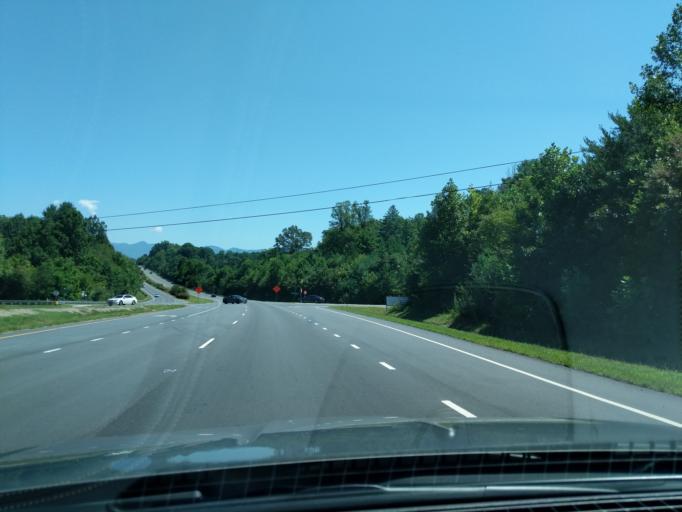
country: US
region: North Carolina
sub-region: Macon County
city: Franklin
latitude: 35.1641
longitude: -83.4176
